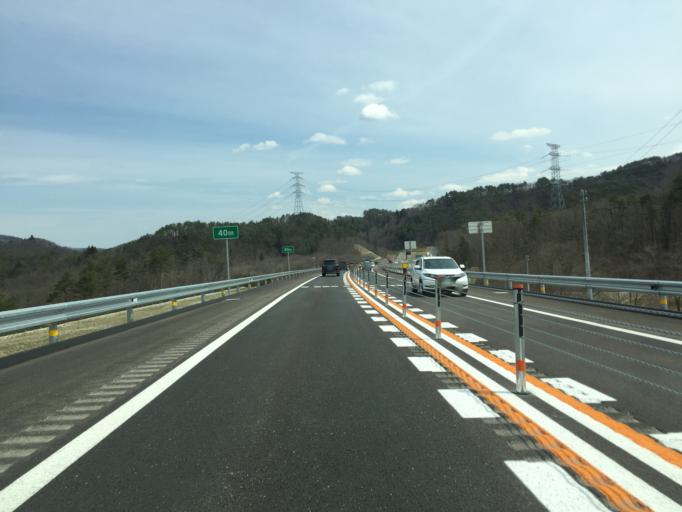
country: JP
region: Yamagata
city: Kaminoyama
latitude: 38.1055
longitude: 140.2214
